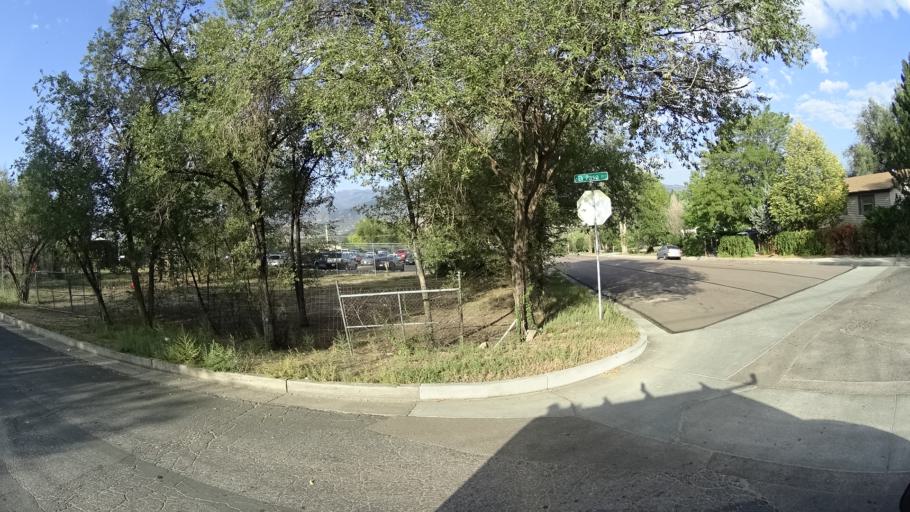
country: US
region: Colorado
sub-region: El Paso County
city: Colorado Springs
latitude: 38.8200
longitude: -104.8132
